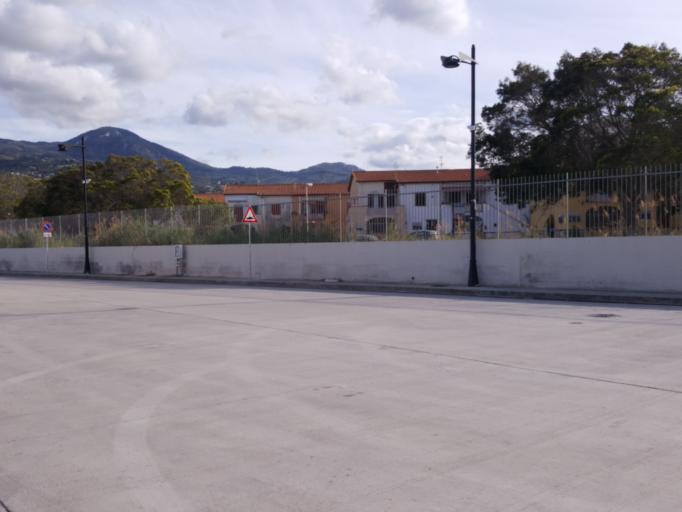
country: IT
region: Sicily
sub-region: Palermo
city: Termini Imerese
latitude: 37.9872
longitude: 13.7028
